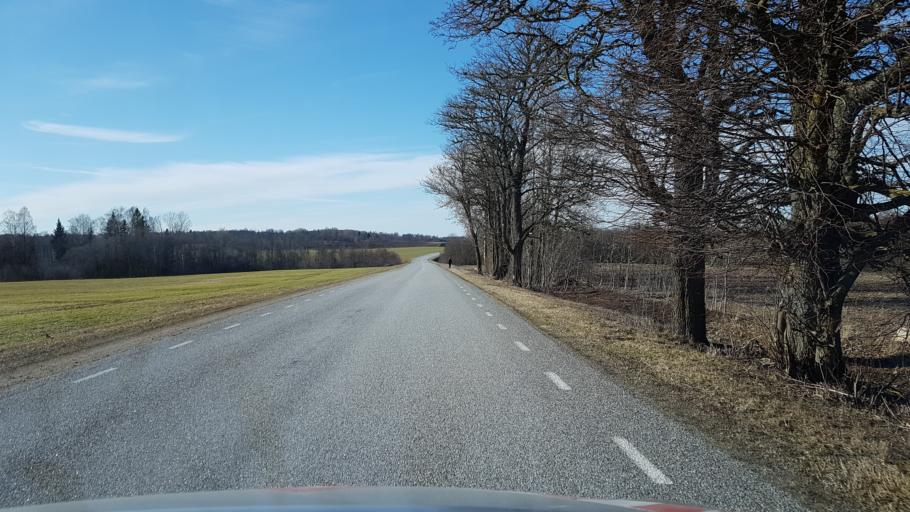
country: EE
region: Laeaene-Virumaa
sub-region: Kadrina vald
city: Kadrina
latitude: 59.2961
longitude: 26.1688
